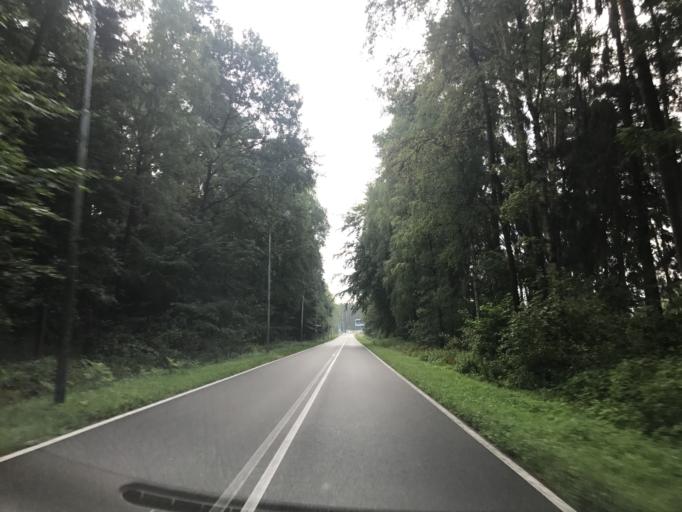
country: PL
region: West Pomeranian Voivodeship
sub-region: Powiat goleniowski
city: Goleniow
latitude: 53.5966
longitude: 14.8903
